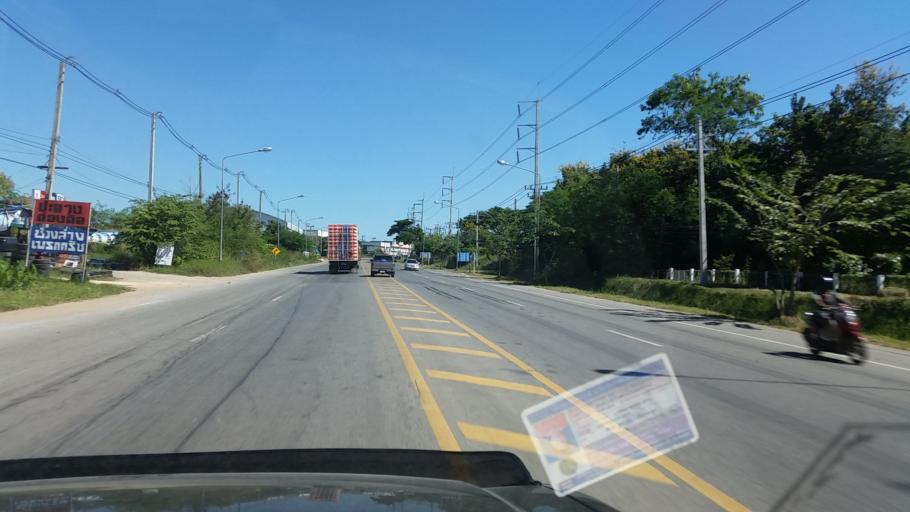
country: TH
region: Chaiyaphum
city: Ban Khwao
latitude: 15.7842
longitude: 101.9080
